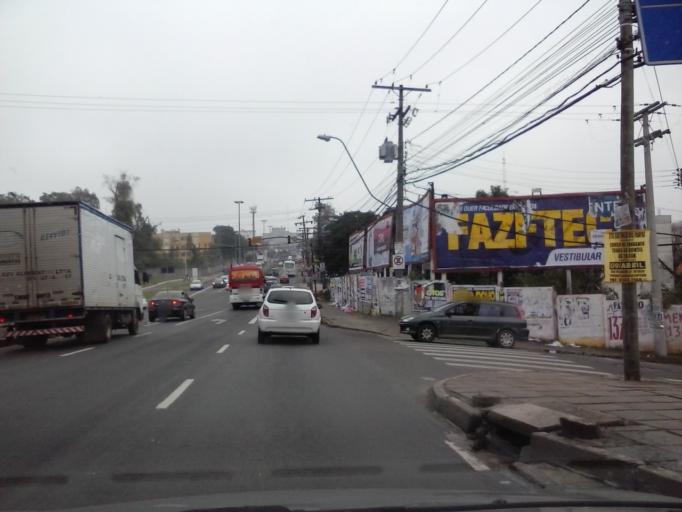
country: BR
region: Rio Grande do Sul
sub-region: Porto Alegre
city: Porto Alegre
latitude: -30.0438
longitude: -51.1423
